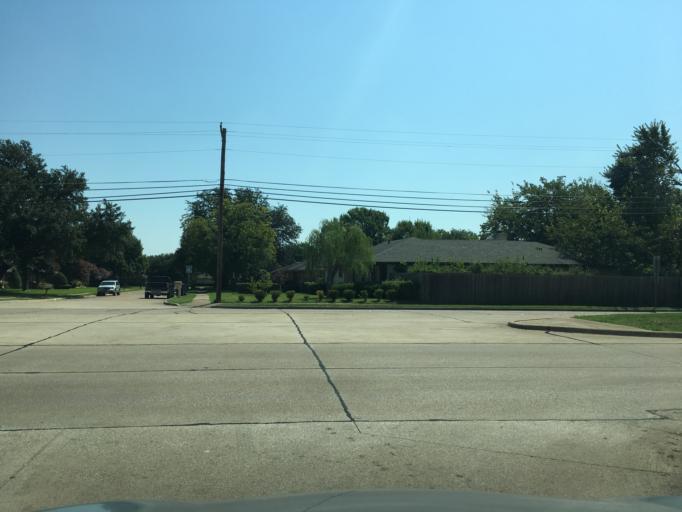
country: US
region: Texas
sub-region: Dallas County
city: Garland
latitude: 32.9355
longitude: -96.6486
